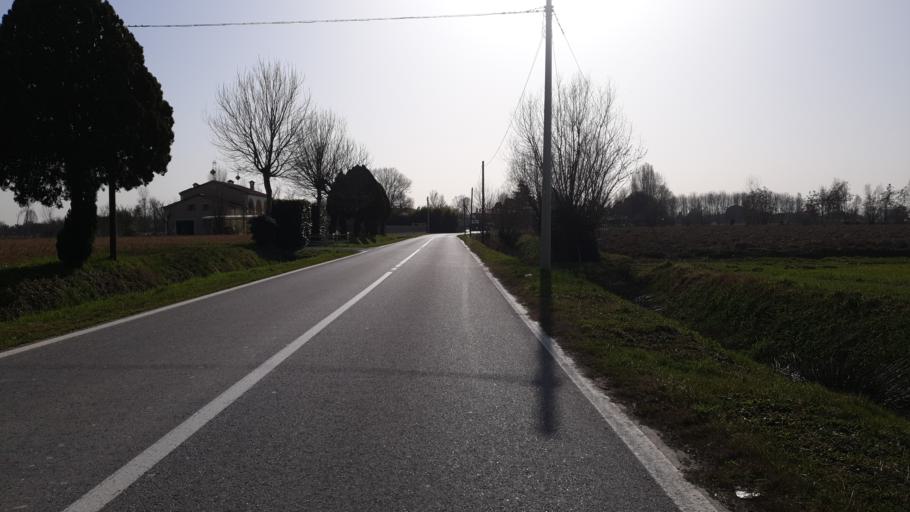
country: IT
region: Veneto
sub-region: Provincia di Padova
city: Saletto
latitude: 45.4840
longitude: 11.8817
